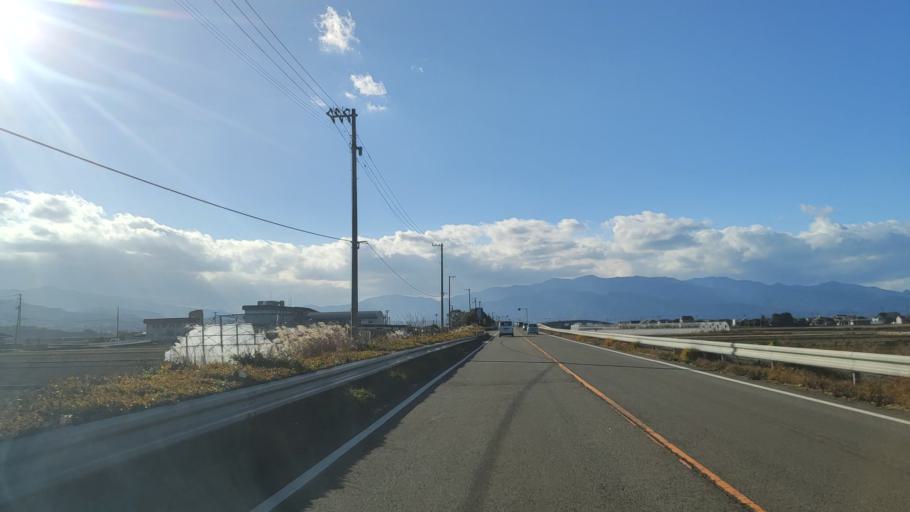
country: JP
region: Ehime
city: Saijo
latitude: 33.9164
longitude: 133.1441
